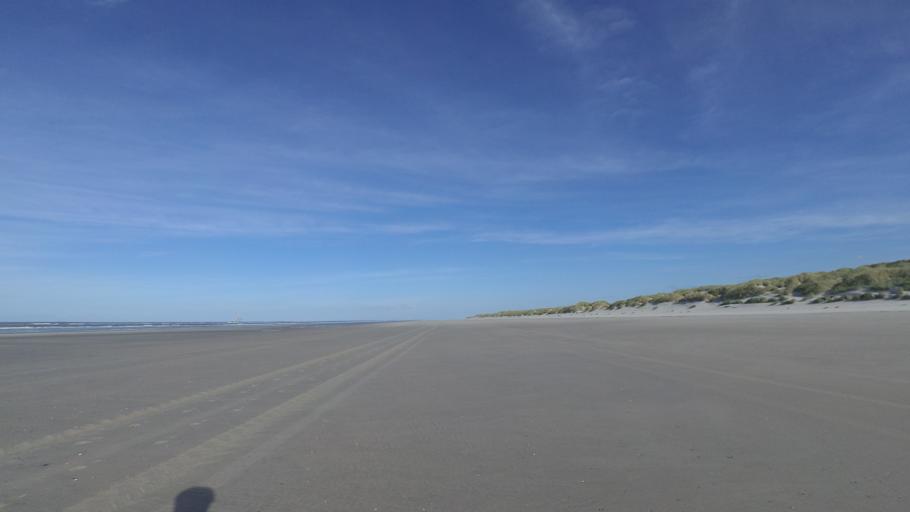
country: NL
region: Friesland
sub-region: Gemeente Ameland
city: Nes
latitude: 53.4657
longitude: 5.8679
